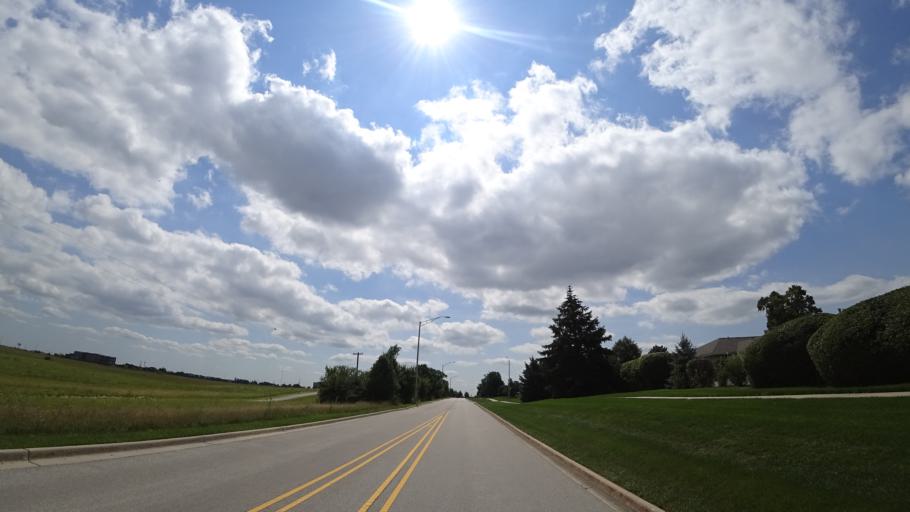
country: US
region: Illinois
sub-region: Will County
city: Mokena
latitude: 41.5594
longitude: -87.8709
